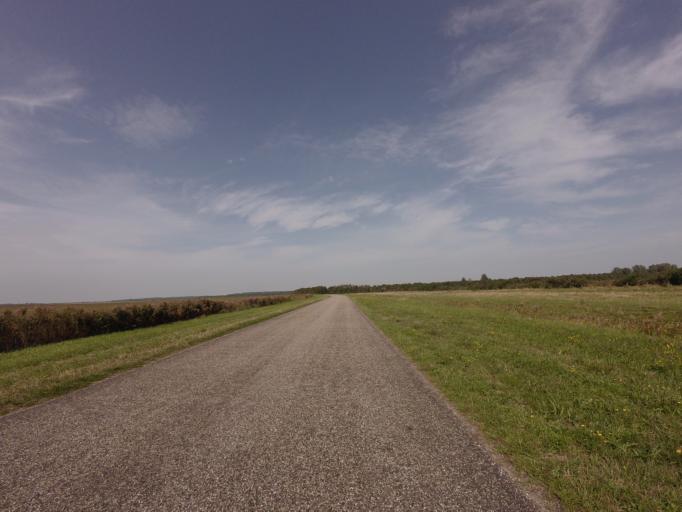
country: NL
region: Groningen
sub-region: Gemeente De Marne
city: Ulrum
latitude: 53.3538
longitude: 6.2651
